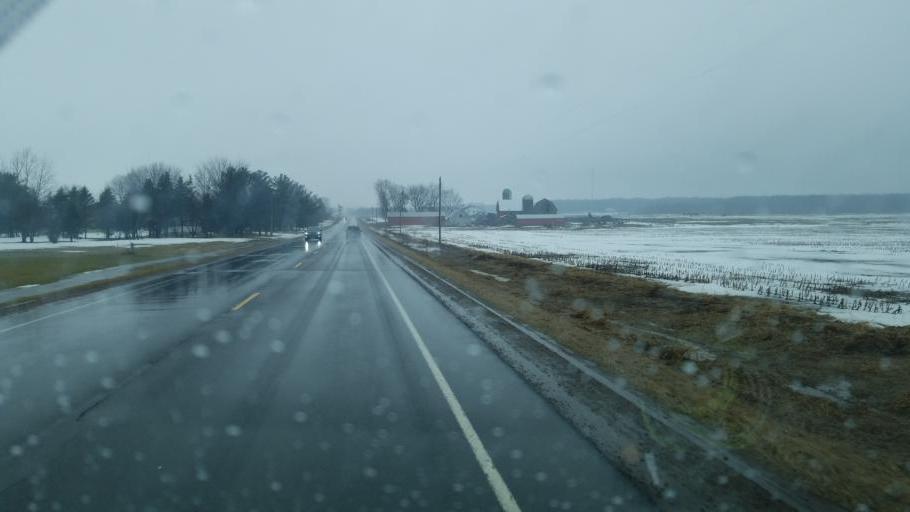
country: US
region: Wisconsin
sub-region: Marathon County
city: Spencer
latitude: 44.6562
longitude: -90.3411
